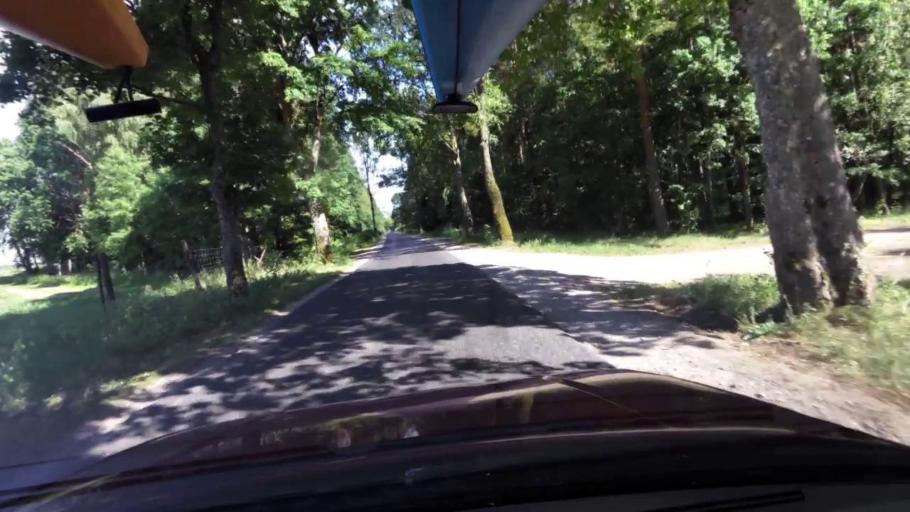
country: PL
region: Pomeranian Voivodeship
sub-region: Powiat bytowski
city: Miastko
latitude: 54.1115
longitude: 16.9591
